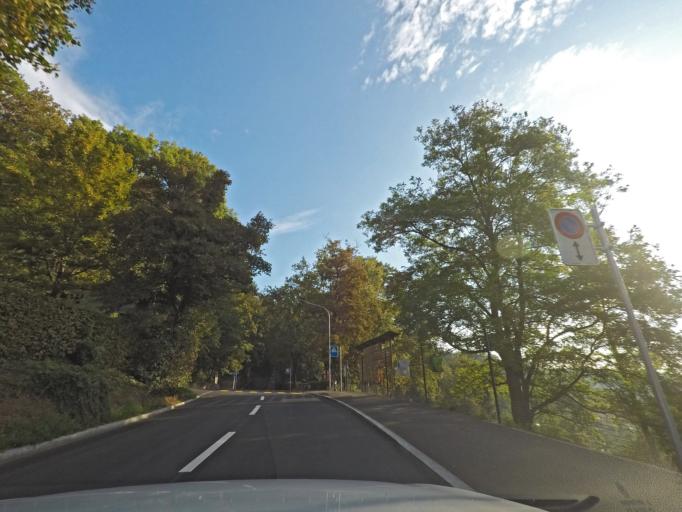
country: CH
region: Zurich
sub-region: Bezirk Zuerich
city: Zuerich (Kreis 10) / Wipkingen
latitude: 47.4002
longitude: 8.5165
